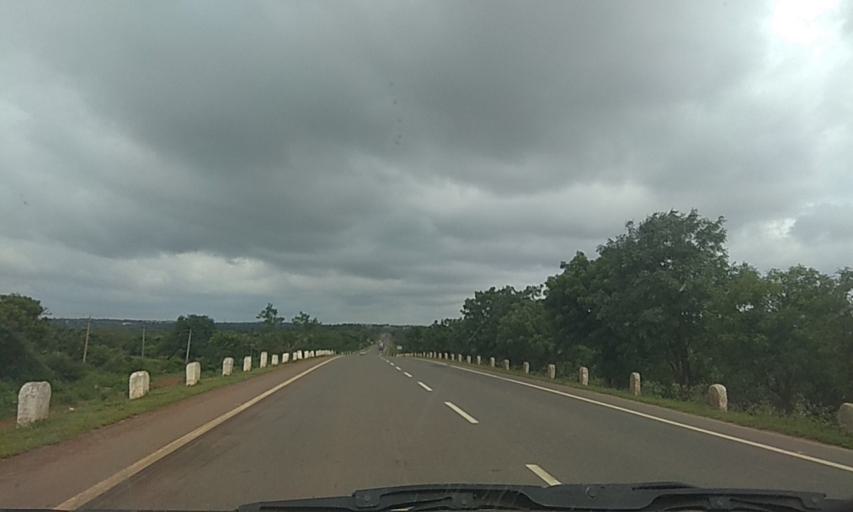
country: IN
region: Karnataka
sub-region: Dharwad
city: Hubli
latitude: 15.3427
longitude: 75.0796
